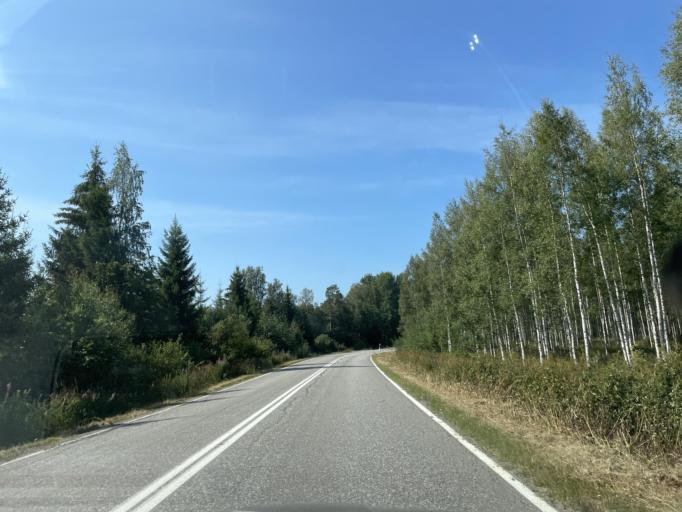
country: FI
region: Central Finland
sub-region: Saarijaervi-Viitasaari
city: Pihtipudas
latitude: 63.3637
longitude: 25.6576
